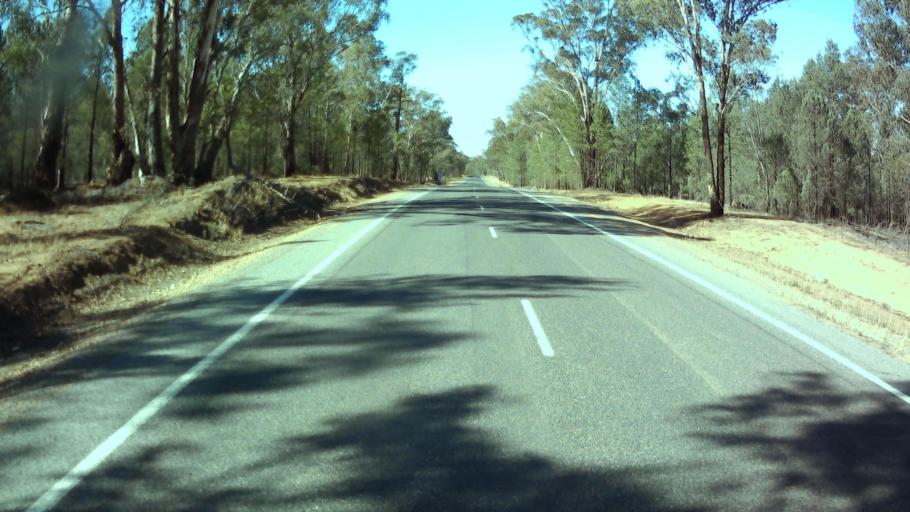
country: AU
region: New South Wales
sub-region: Weddin
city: Grenfell
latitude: -33.7505
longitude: 148.0852
